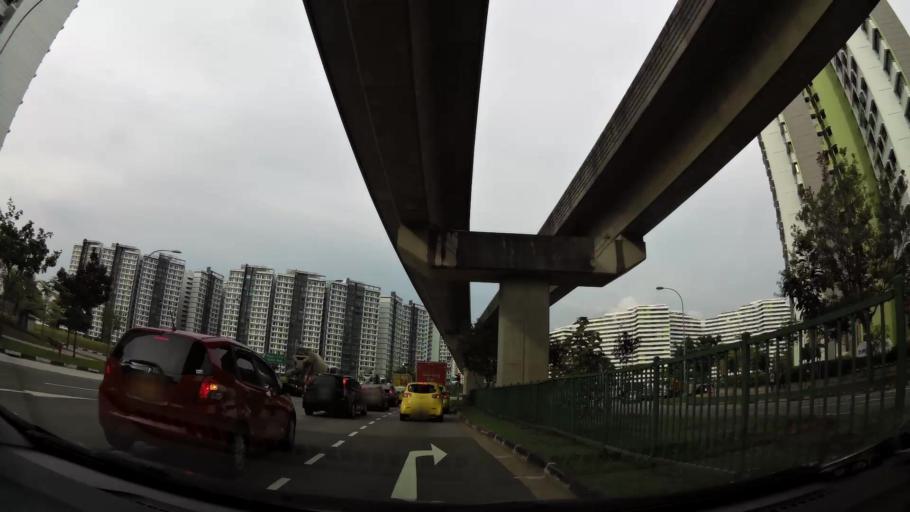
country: MY
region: Johor
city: Kampung Pasir Gudang Baru
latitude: 1.4058
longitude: 103.8973
